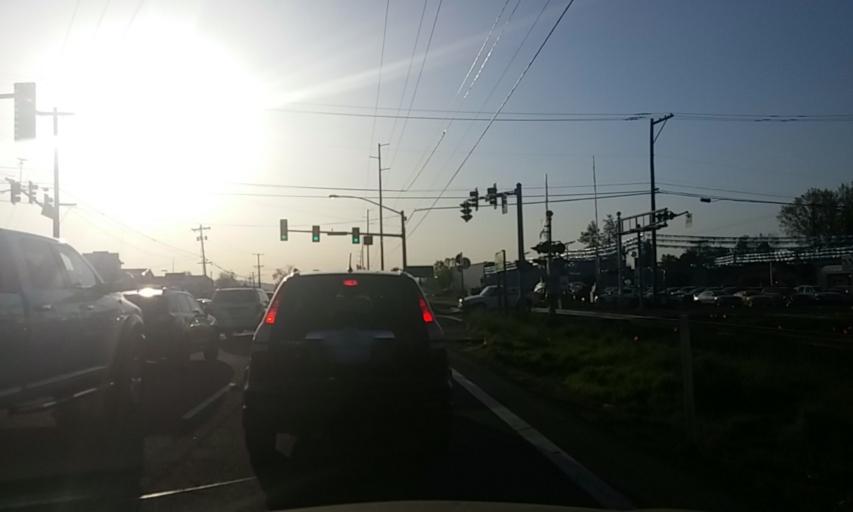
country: US
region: Oregon
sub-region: Washington County
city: Beaverton
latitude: 45.4884
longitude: -122.8153
